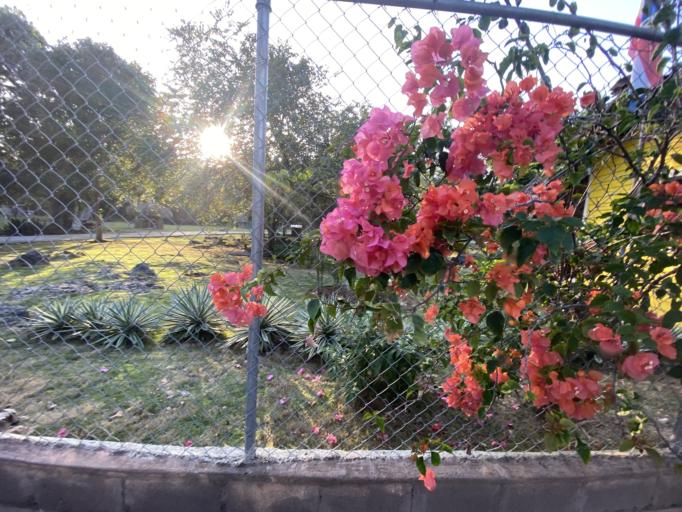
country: DO
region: Maria Trinidad Sanchez
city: La Entrada
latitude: 19.5639
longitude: -69.9073
